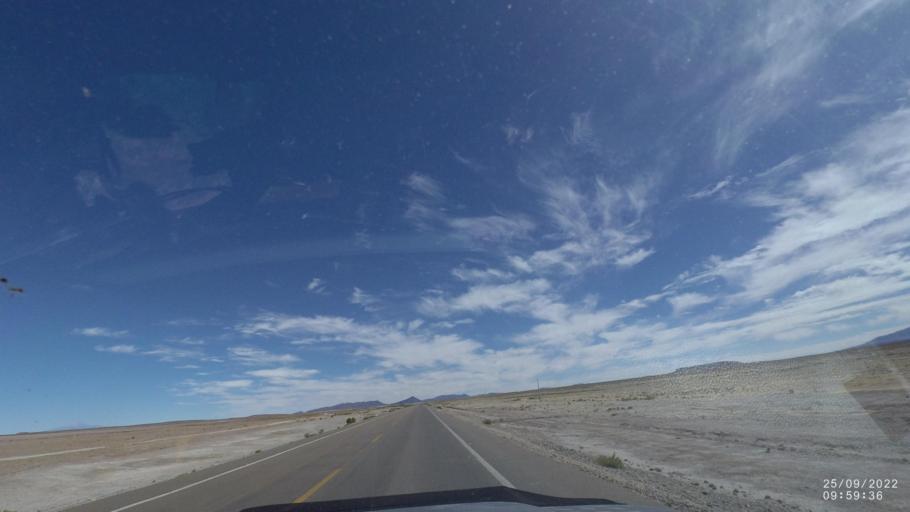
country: BO
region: Potosi
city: Colchani
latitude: -20.2886
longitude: -66.9393
